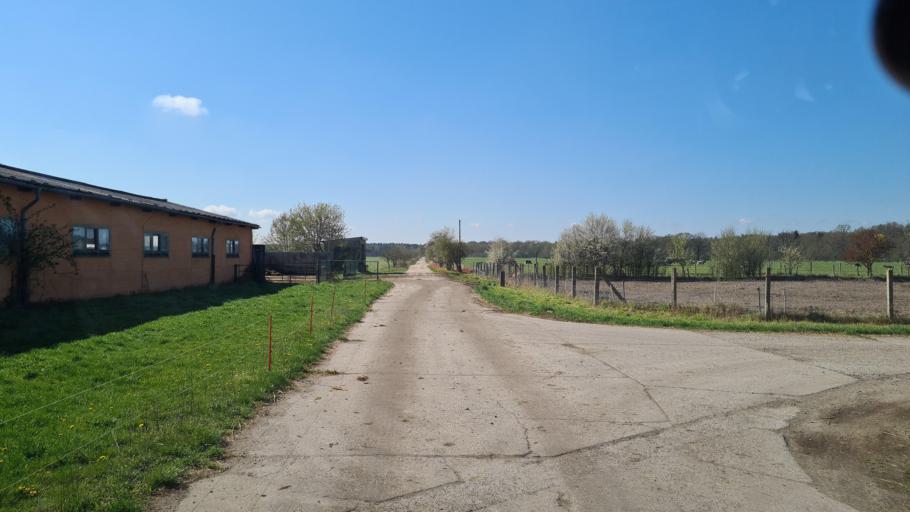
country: DE
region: Brandenburg
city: Altdobern
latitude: 51.7104
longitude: 14.0457
